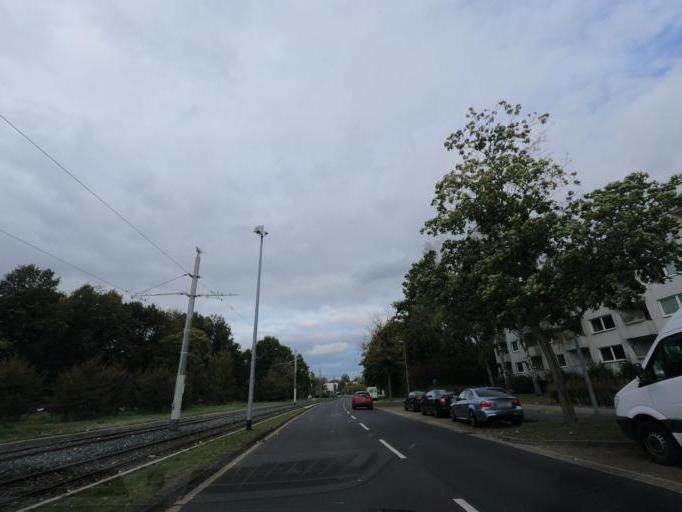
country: DE
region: Lower Saxony
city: Leiferde
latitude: 52.2425
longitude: 10.4889
